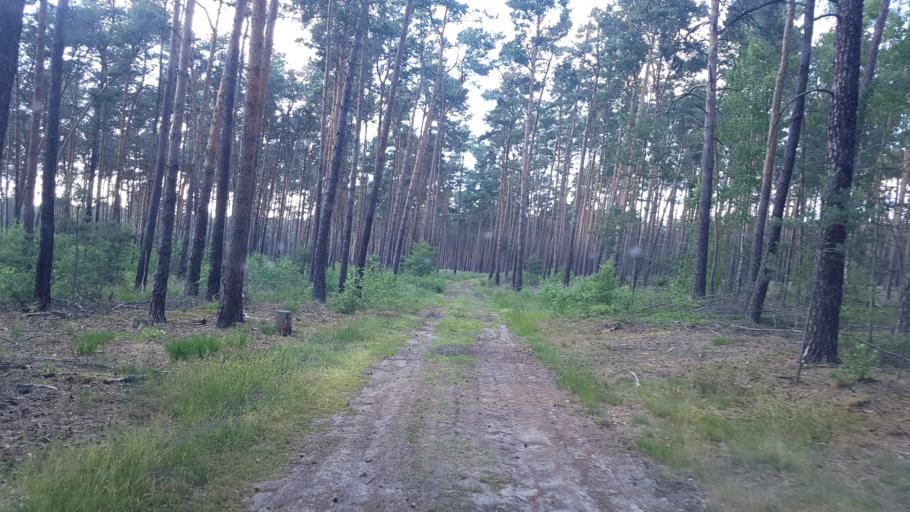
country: DE
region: Brandenburg
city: Trobitz
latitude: 51.6423
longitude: 13.4158
